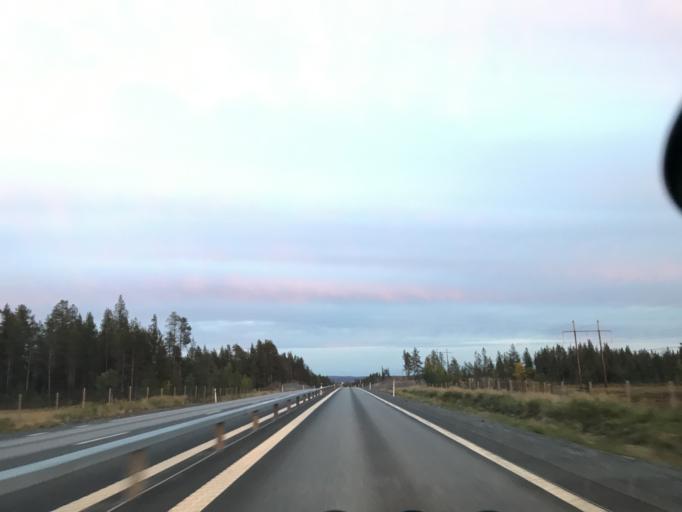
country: SE
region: Norrbotten
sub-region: Gallivare Kommun
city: Malmberget
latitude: 67.6835
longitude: 20.8653
